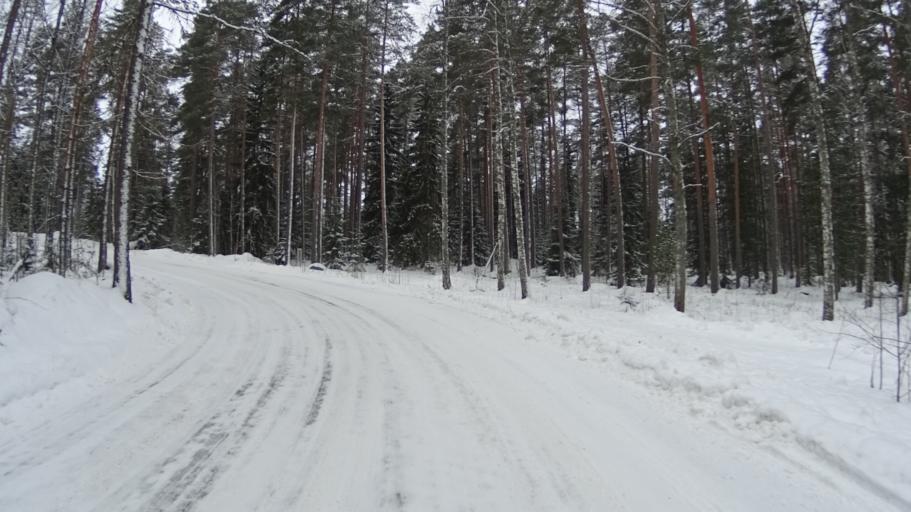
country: FI
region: Uusimaa
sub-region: Helsinki
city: Vihti
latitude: 60.3579
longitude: 24.2266
